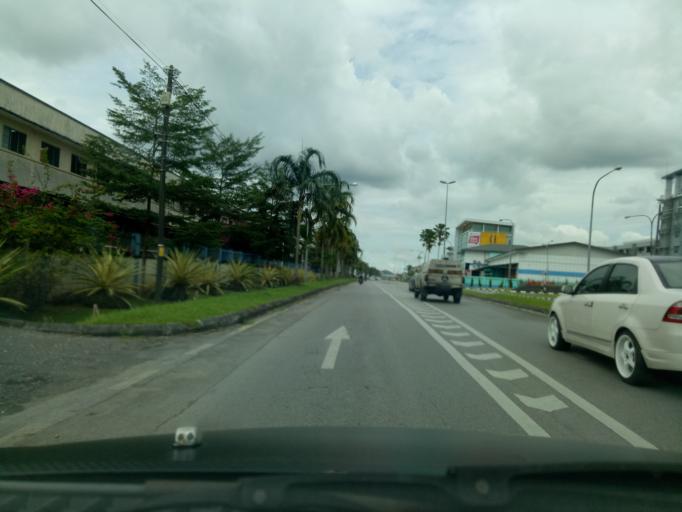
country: MY
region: Sarawak
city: Kuching
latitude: 1.5526
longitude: 110.3718
